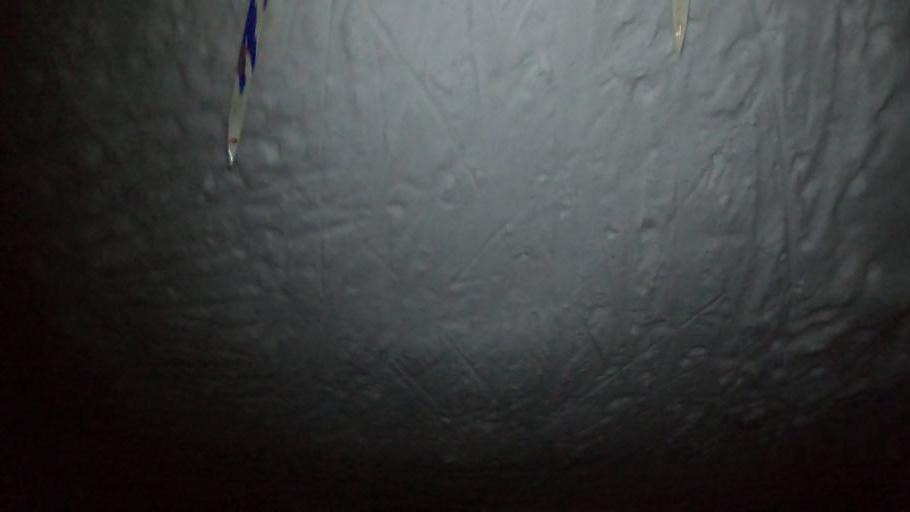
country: RU
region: Moskovskaya
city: Opalikha
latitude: 55.8629
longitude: 37.2334
